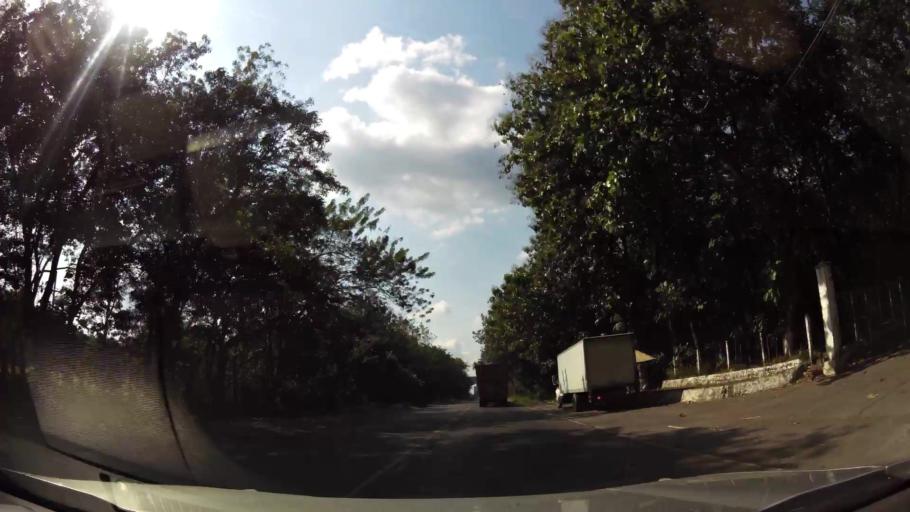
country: GT
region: Retalhuleu
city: San Sebastian
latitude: 14.5517
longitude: -91.6356
